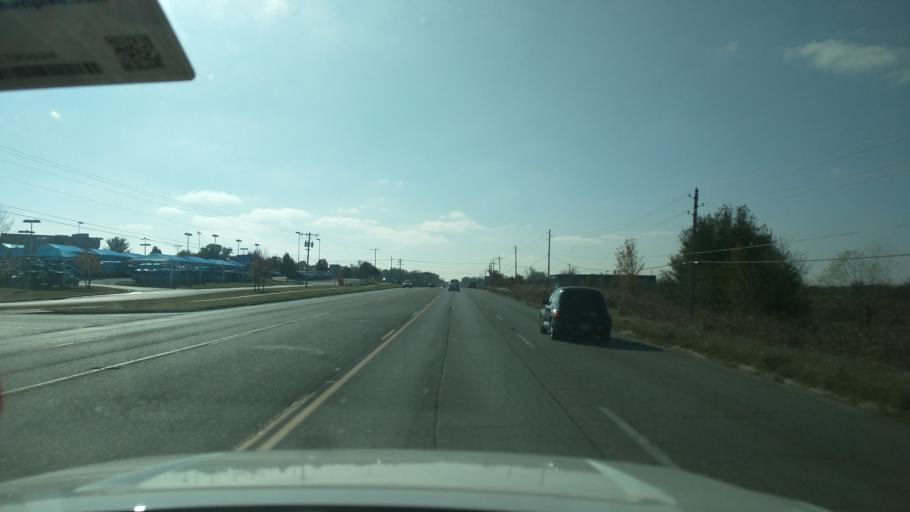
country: US
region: Oklahoma
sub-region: Washington County
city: Bartlesville
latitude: 36.7020
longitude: -95.9352
